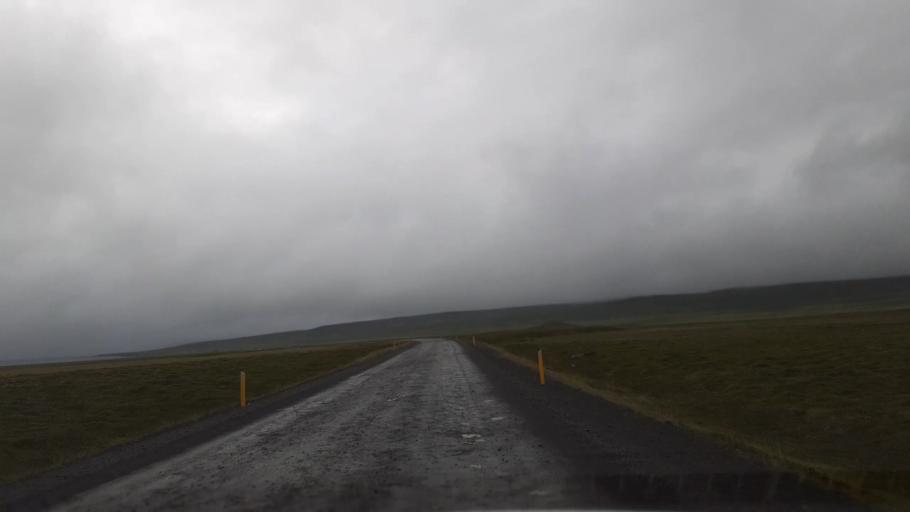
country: IS
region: East
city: Egilsstadir
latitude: 66.0340
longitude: -15.0589
